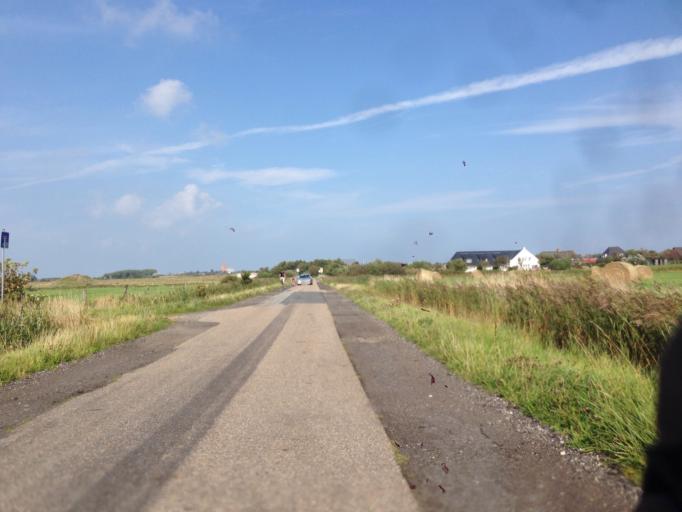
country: DE
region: Schleswig-Holstein
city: Keitum
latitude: 54.8891
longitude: 8.3534
